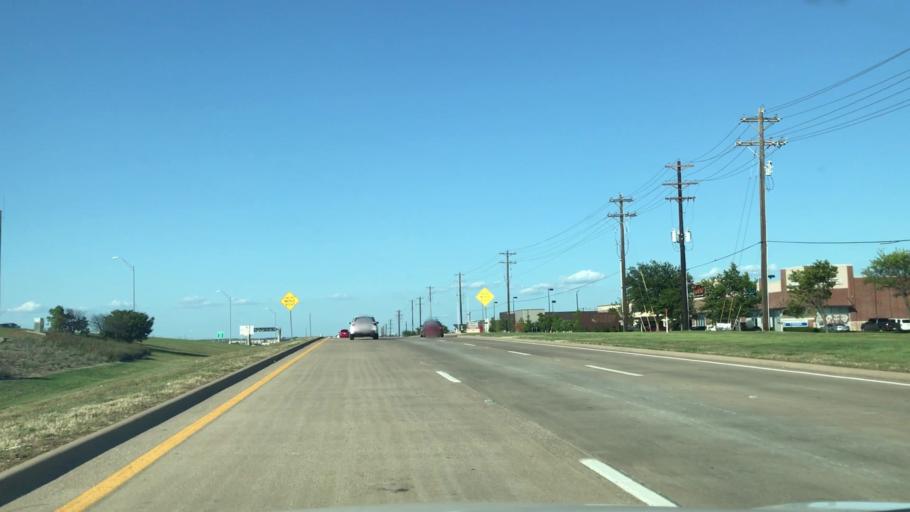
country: US
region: Texas
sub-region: Collin County
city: Frisco
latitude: 33.1121
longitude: -96.7668
